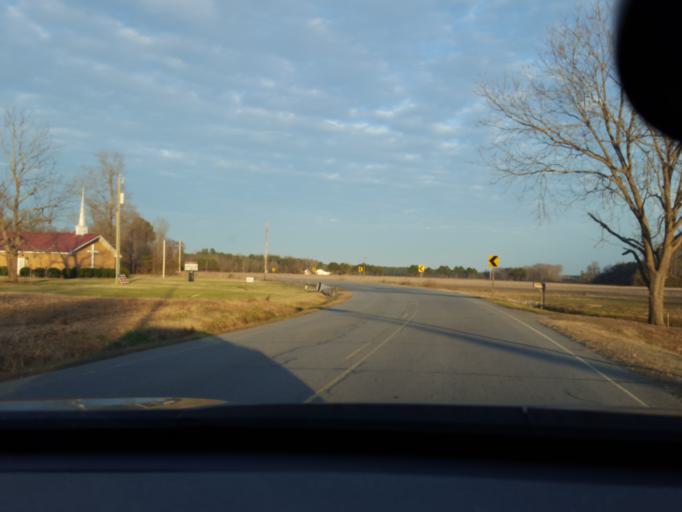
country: US
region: North Carolina
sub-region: Hertford County
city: Murfreesboro
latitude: 36.2719
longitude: -77.2239
